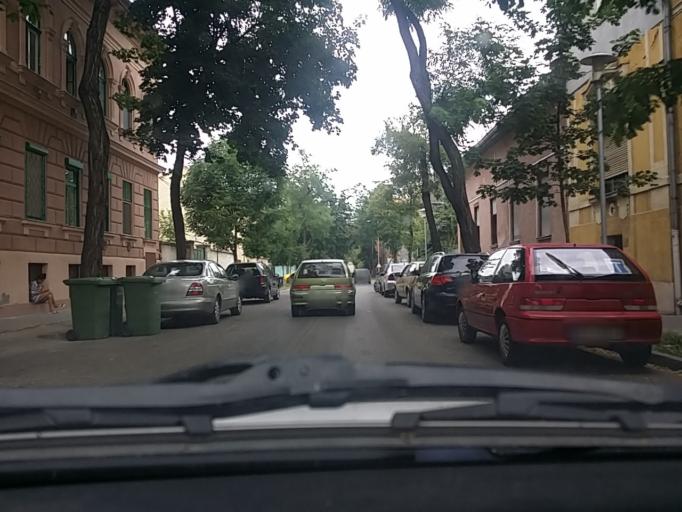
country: HU
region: Budapest
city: Budapest X. keruelet
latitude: 47.4873
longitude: 19.1306
